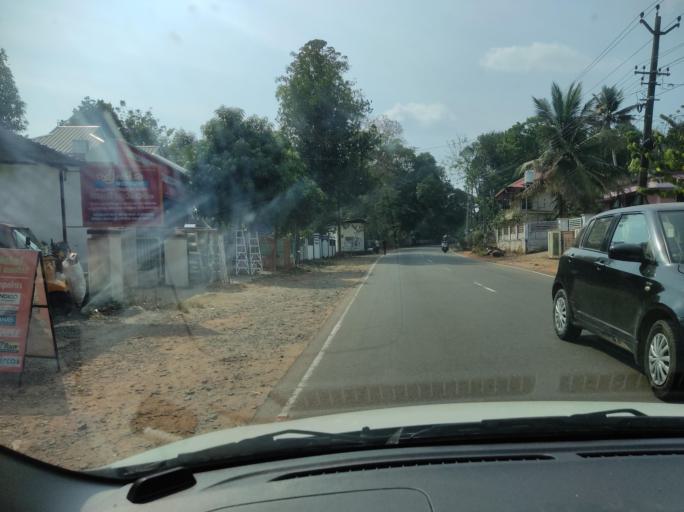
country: IN
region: Kerala
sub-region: Kottayam
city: Kottayam
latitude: 9.6758
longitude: 76.5130
